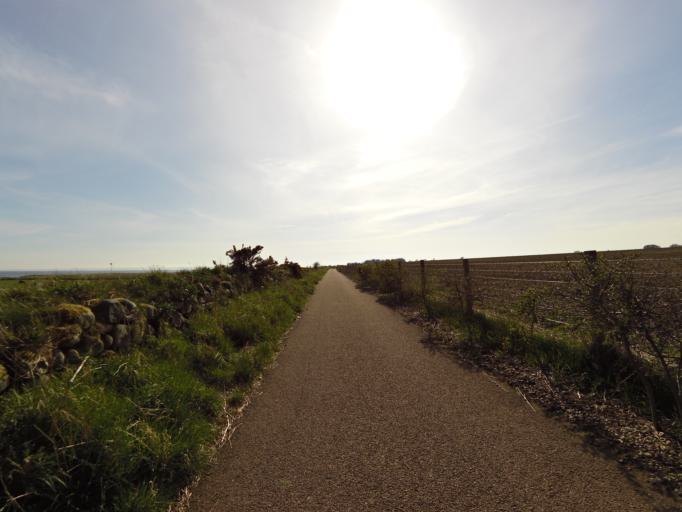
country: GB
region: Scotland
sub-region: Angus
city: Carnoustie
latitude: 56.5126
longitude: -2.6737
